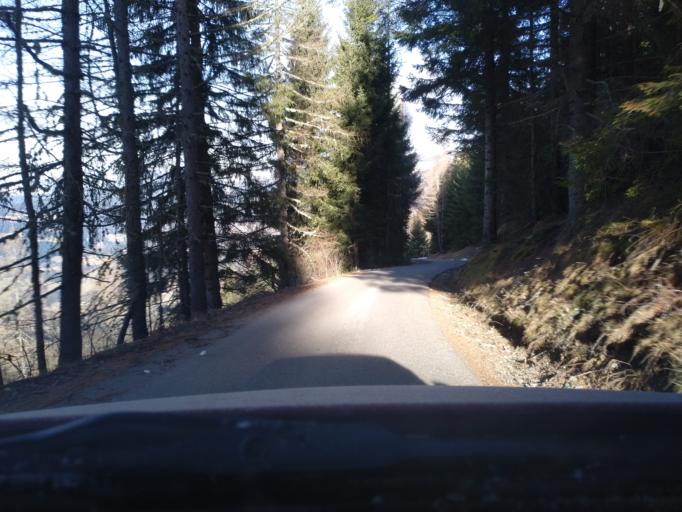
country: AT
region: Carinthia
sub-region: Politischer Bezirk Villach Land
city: Arriach
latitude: 46.7101
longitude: 13.8935
